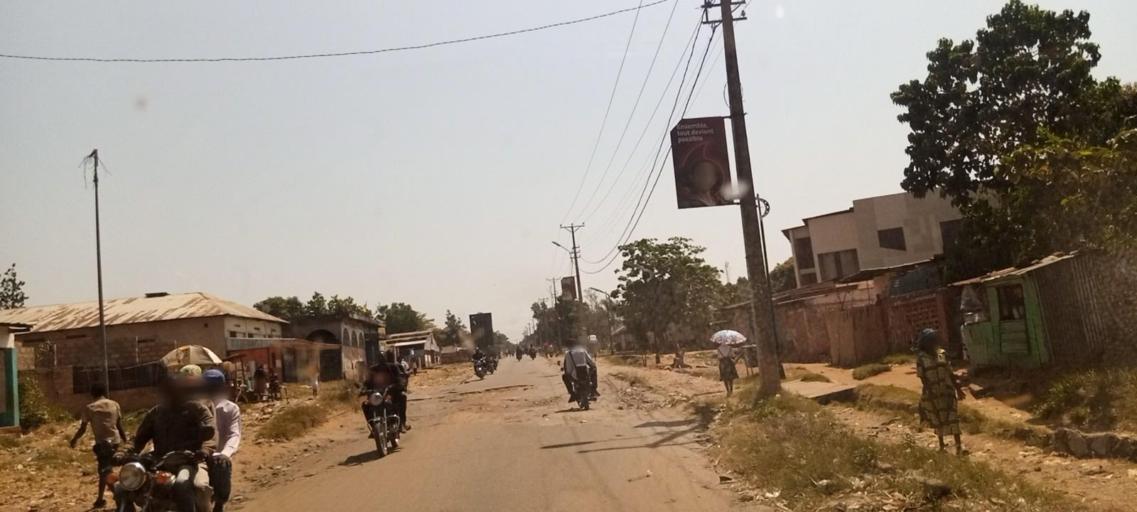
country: CD
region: Kasai-Oriental
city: Mbuji-Mayi
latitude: -6.1244
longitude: 23.5973
